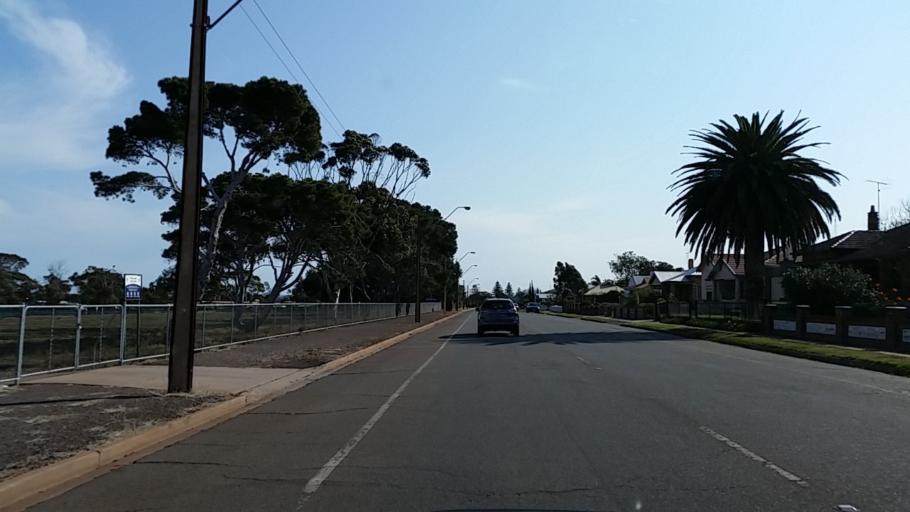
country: AU
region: South Australia
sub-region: Whyalla
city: Whyalla
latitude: -33.0400
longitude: 137.5800
